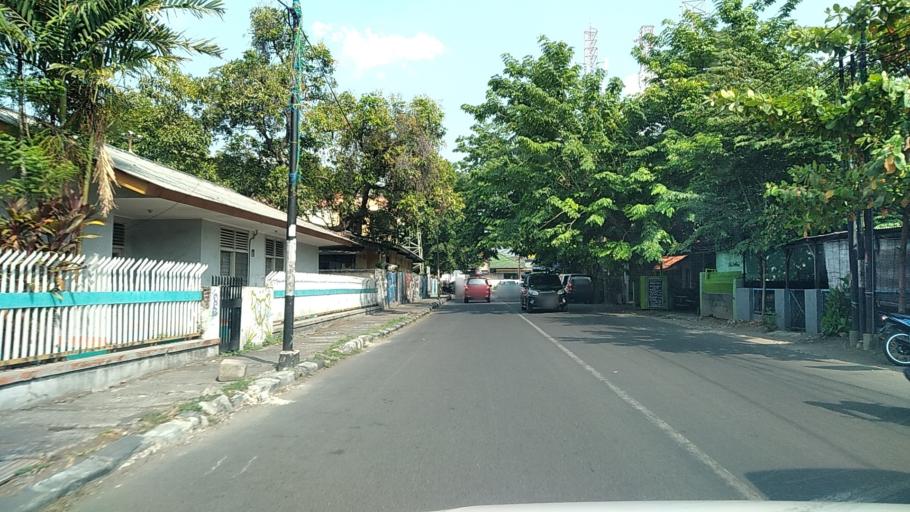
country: ID
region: Central Java
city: Semarang
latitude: -6.9955
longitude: 110.4242
